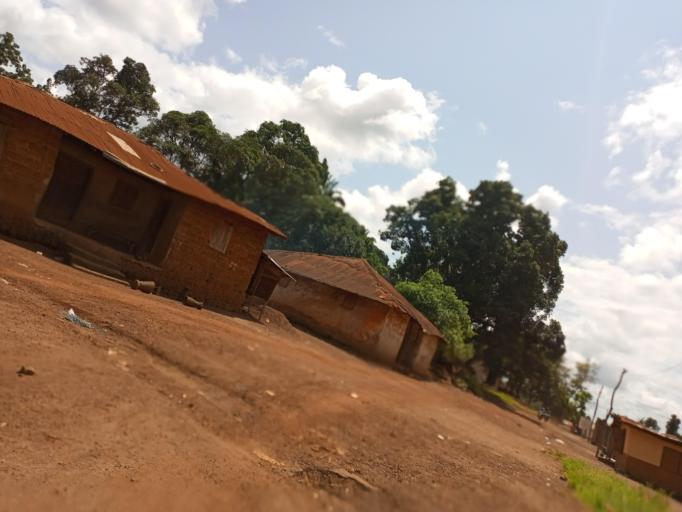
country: SL
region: Northern Province
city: Kamakwie
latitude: 9.4983
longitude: -12.2383
